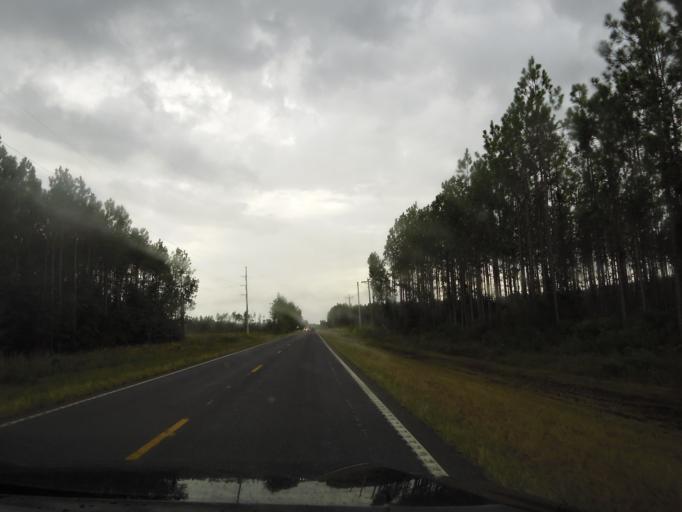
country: US
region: Florida
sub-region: Nassau County
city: Hilliard
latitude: 30.5609
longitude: -82.0429
